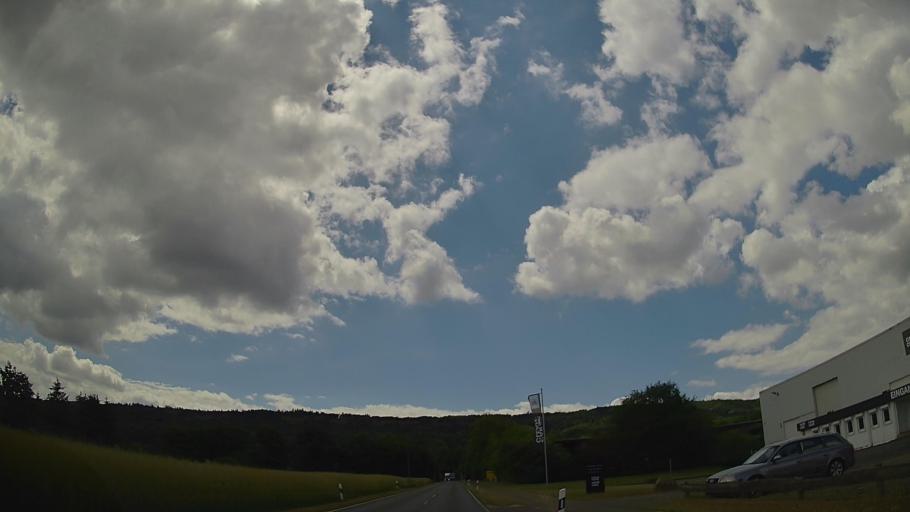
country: DE
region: North Rhine-Westphalia
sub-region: Regierungsbezirk Detmold
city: Minden
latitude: 52.2657
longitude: 8.8505
